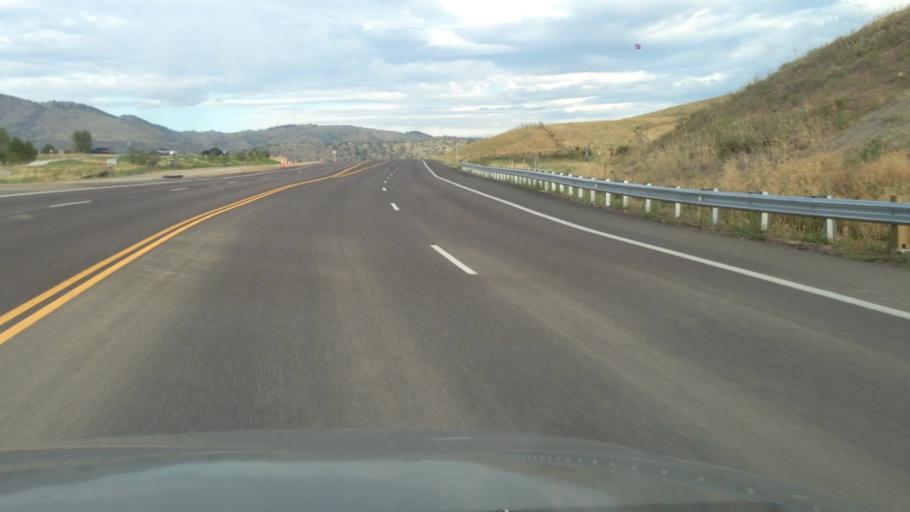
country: US
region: Colorado
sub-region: Jefferson County
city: West Pleasant View
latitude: 39.6803
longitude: -105.1664
